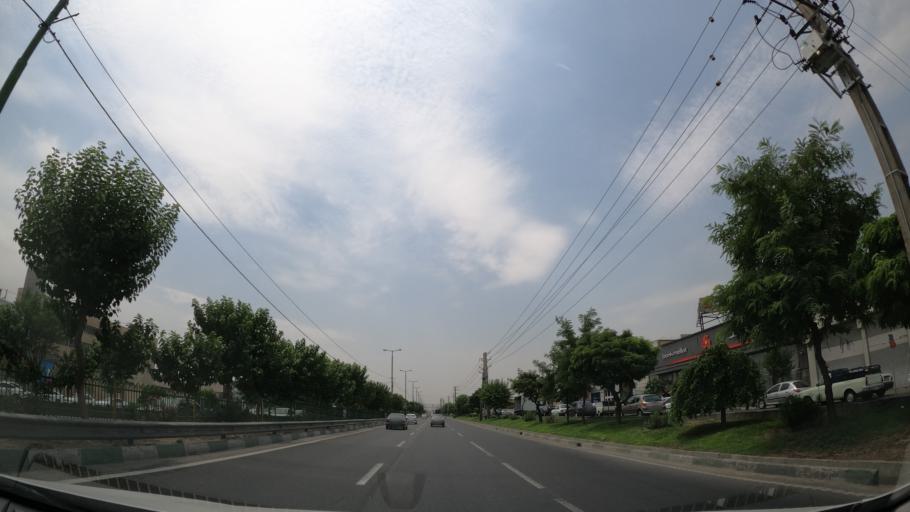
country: IR
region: Tehran
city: Tehran
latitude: 35.6763
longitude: 51.2924
